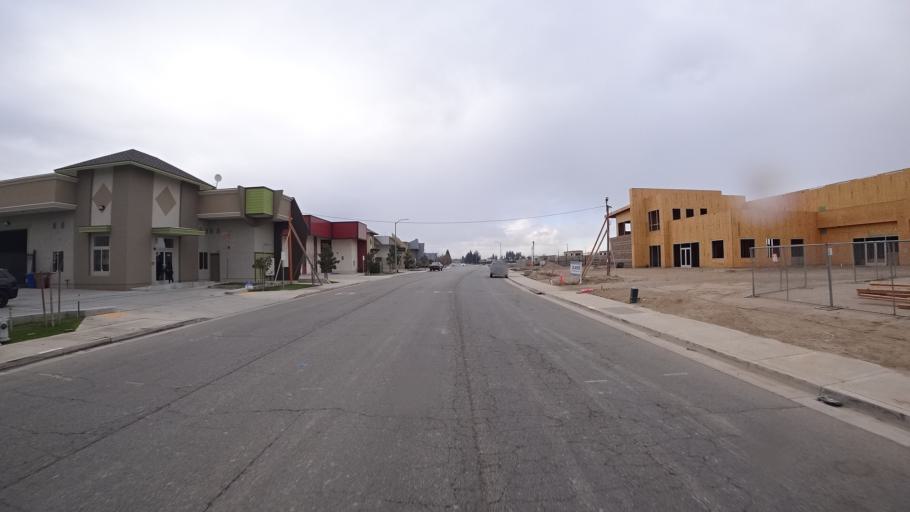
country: US
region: California
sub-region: Kern County
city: Greenfield
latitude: 35.3084
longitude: -119.0673
